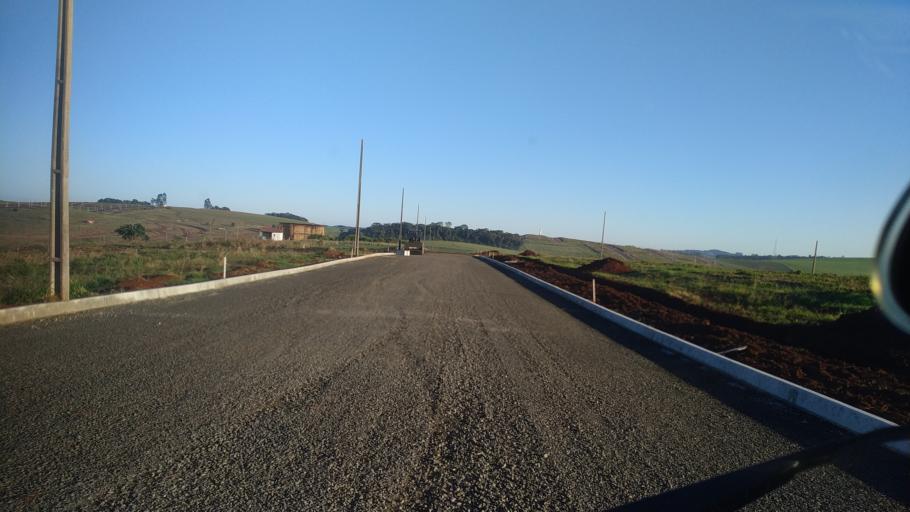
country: BR
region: Santa Catarina
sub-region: Chapeco
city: Chapeco
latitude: -27.0866
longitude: -52.6960
